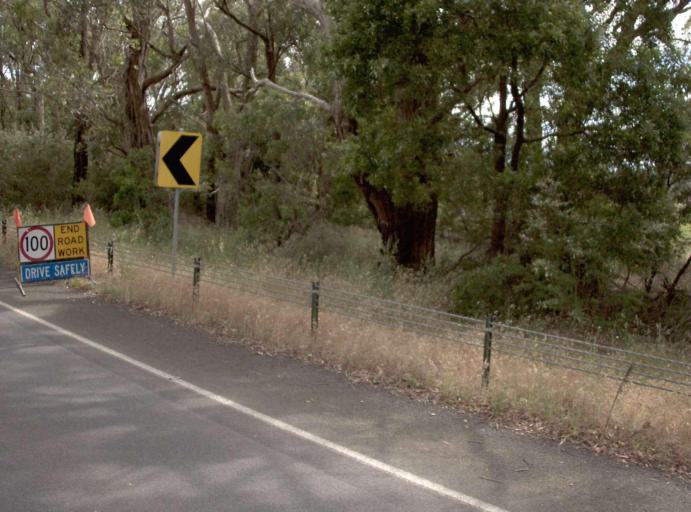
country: AU
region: Victoria
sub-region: Latrobe
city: Moe
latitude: -38.0858
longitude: 146.1993
